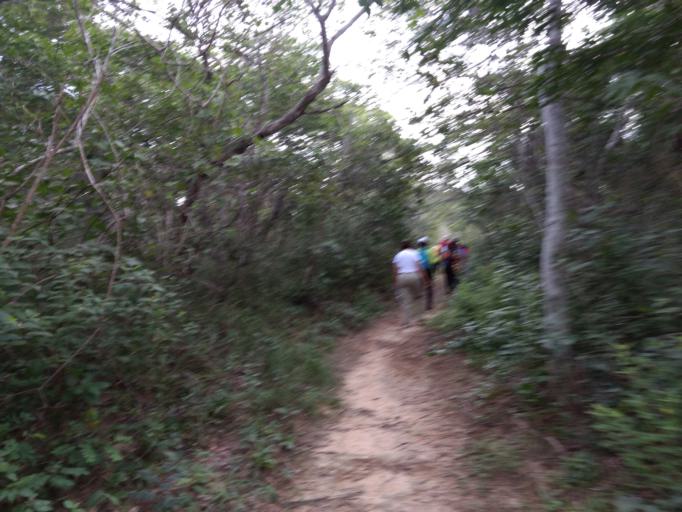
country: BR
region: Ceara
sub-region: Crateus
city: Crateus
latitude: -5.1448
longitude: -40.9235
